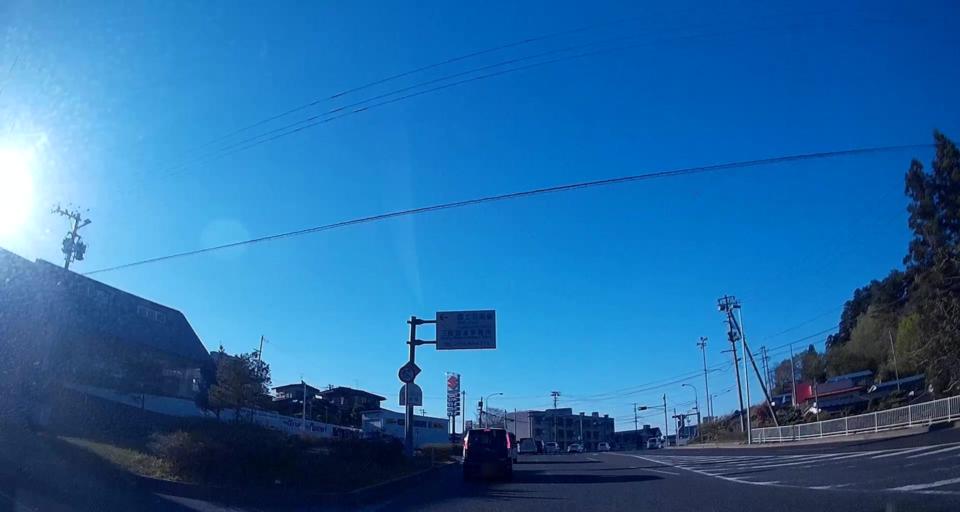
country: JP
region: Iwate
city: Miyako
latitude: 39.6159
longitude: 141.9614
